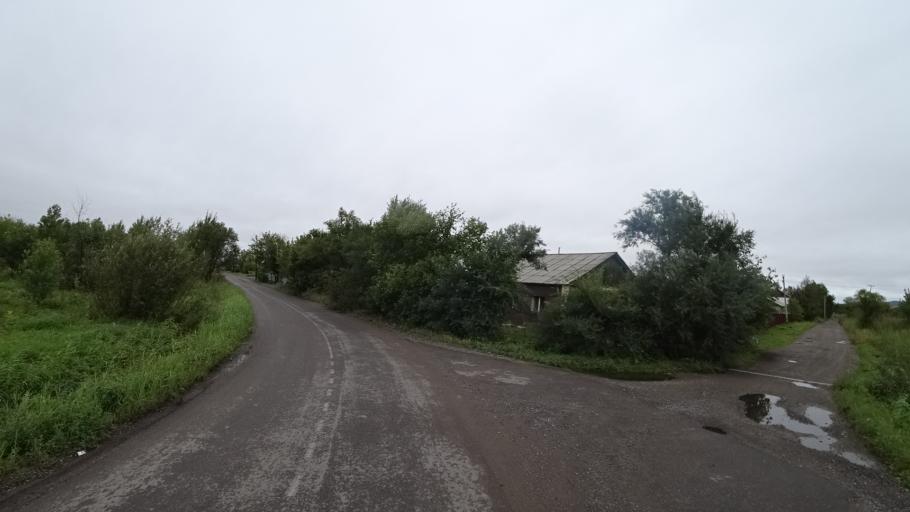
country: RU
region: Primorskiy
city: Monastyrishche
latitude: 44.2100
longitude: 132.4380
